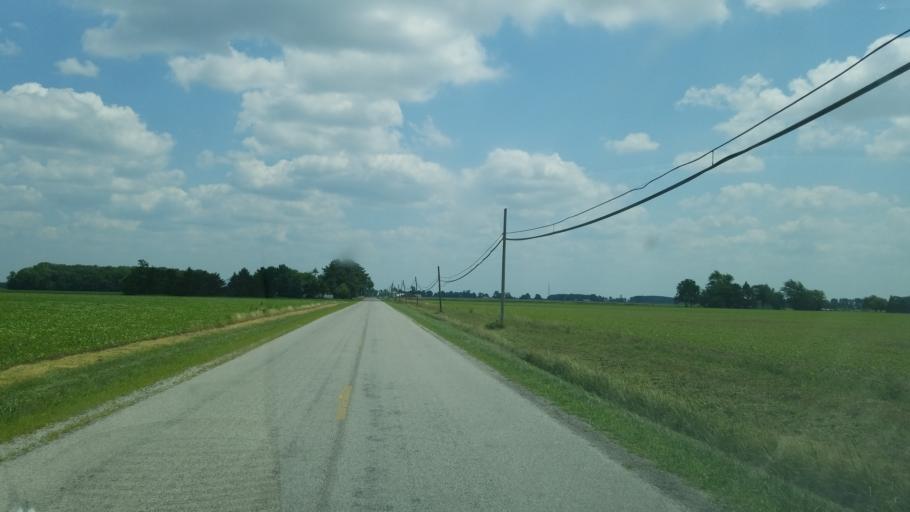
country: US
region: Ohio
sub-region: Henry County
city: Liberty Center
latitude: 41.3418
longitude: -84.0234
